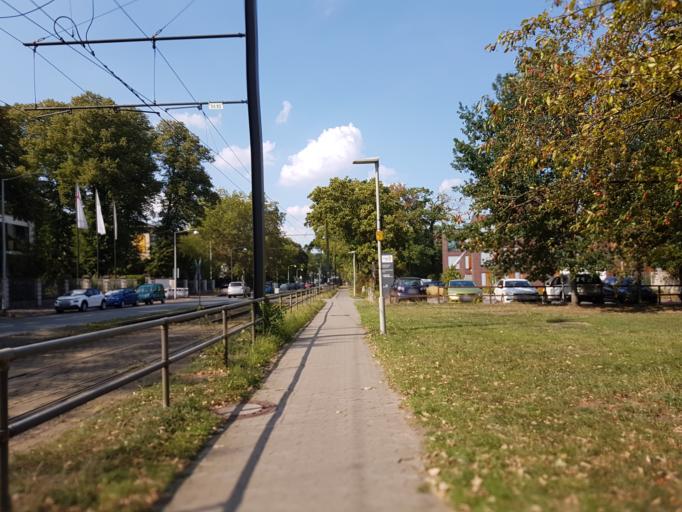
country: DE
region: Lower Saxony
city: Hannover
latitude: 52.3783
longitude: 9.7685
